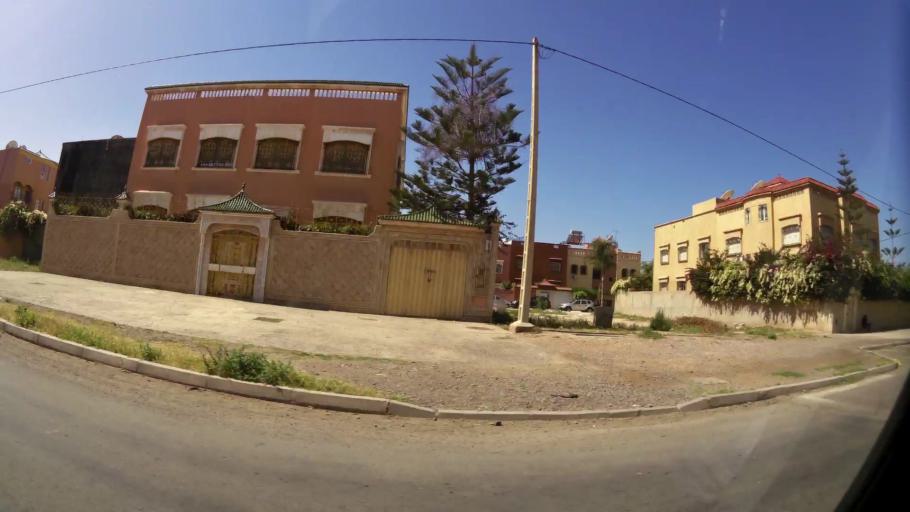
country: MA
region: Souss-Massa-Draa
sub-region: Inezgane-Ait Mellou
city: Inezgane
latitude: 30.3269
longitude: -9.5068
